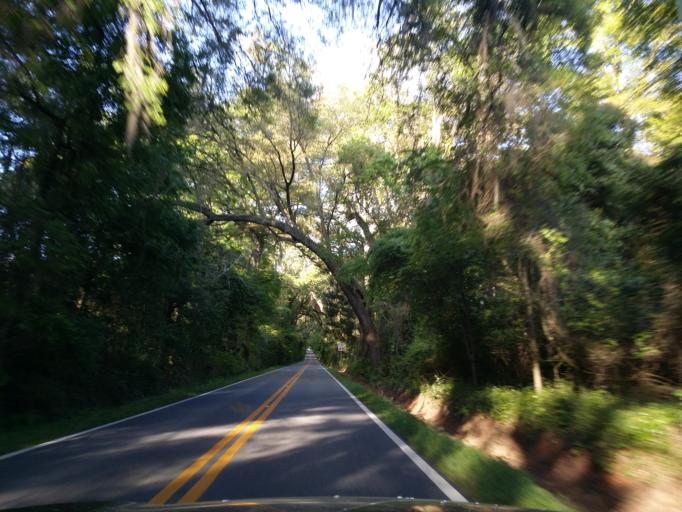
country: US
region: Florida
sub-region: Leon County
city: Tallahassee
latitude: 30.4868
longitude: -84.1933
